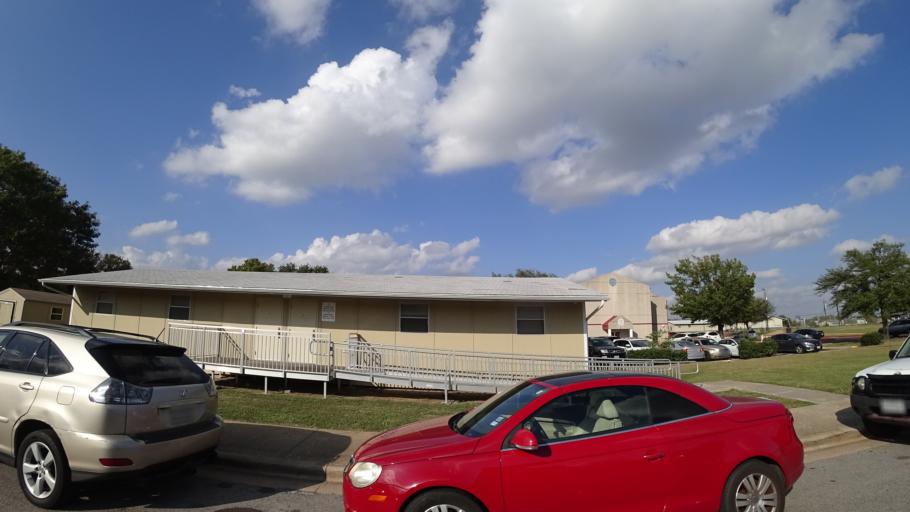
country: US
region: Texas
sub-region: Williamson County
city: Round Rock
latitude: 30.4981
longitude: -97.6741
